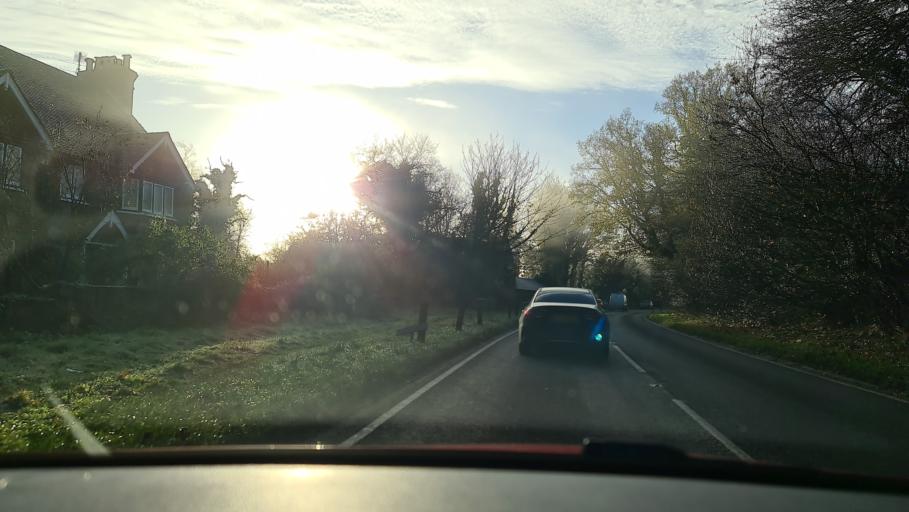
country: GB
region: England
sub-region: Buckinghamshire
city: Wendover
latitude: 51.7489
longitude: -0.7341
